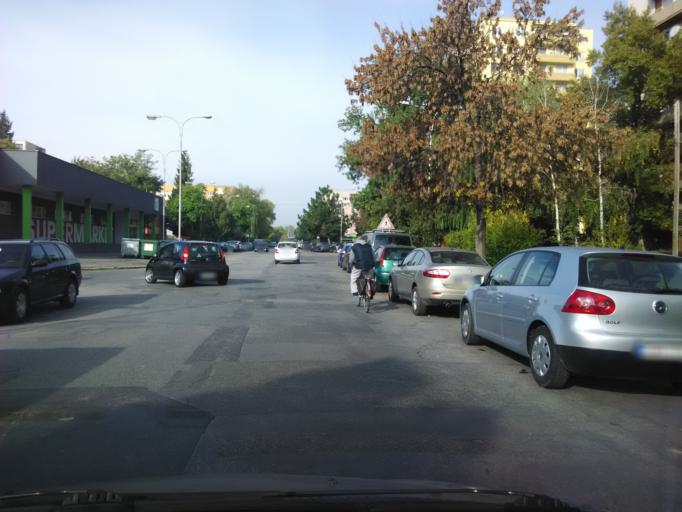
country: SK
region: Nitriansky
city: Komarno
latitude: 47.7625
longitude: 18.1143
